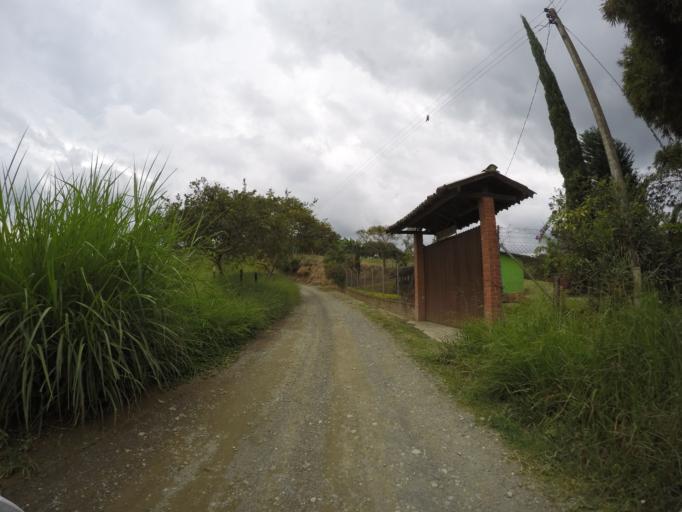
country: CO
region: Quindio
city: Circasia
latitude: 4.6299
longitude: -75.6843
